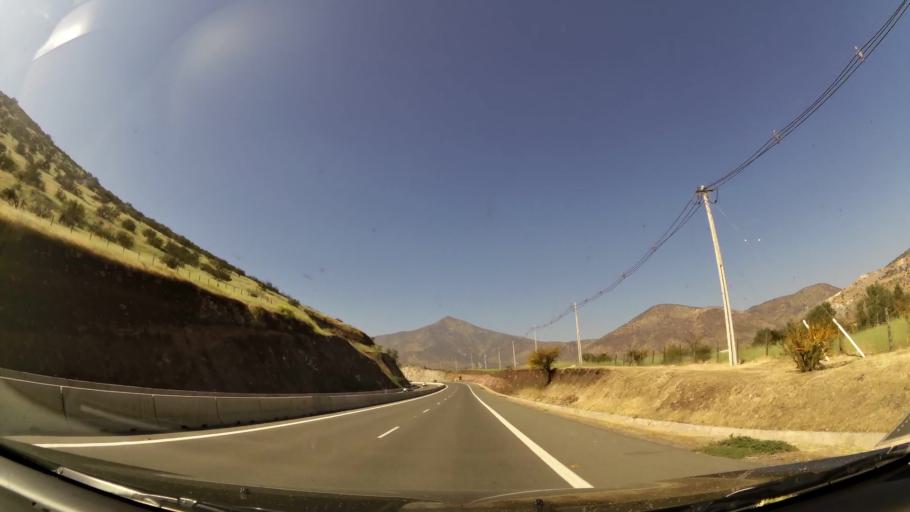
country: CL
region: Santiago Metropolitan
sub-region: Provincia de Chacabuco
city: Chicureo Abajo
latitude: -33.3080
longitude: -70.6538
